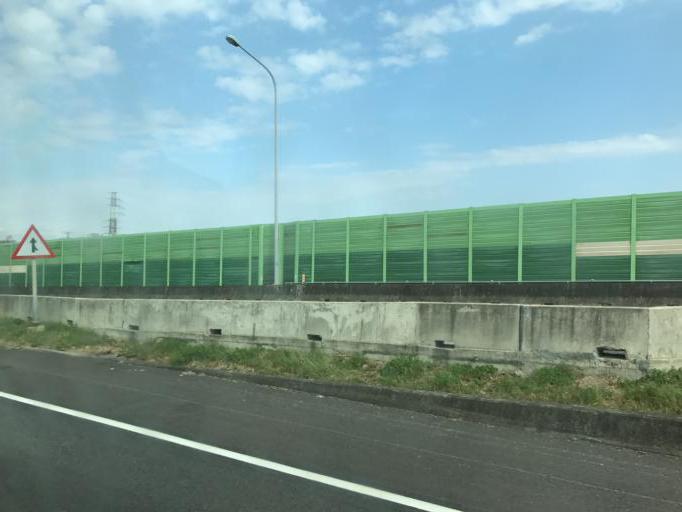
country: TW
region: Taiwan
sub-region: Hsinchu
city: Zhubei
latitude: 24.8020
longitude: 121.0094
